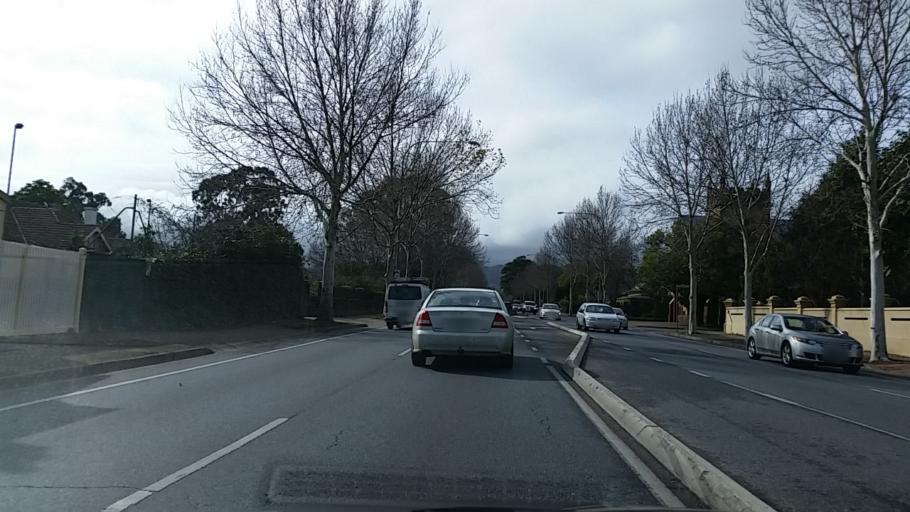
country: AU
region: South Australia
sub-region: Unley
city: Unley Park
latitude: -34.9657
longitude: 138.6026
